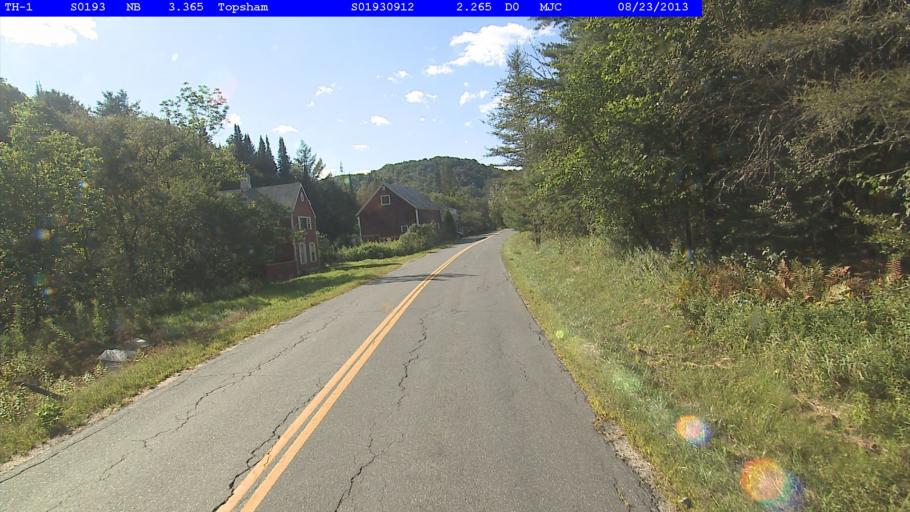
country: US
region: New Hampshire
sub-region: Grafton County
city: Haverhill
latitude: 44.1011
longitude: -72.2282
